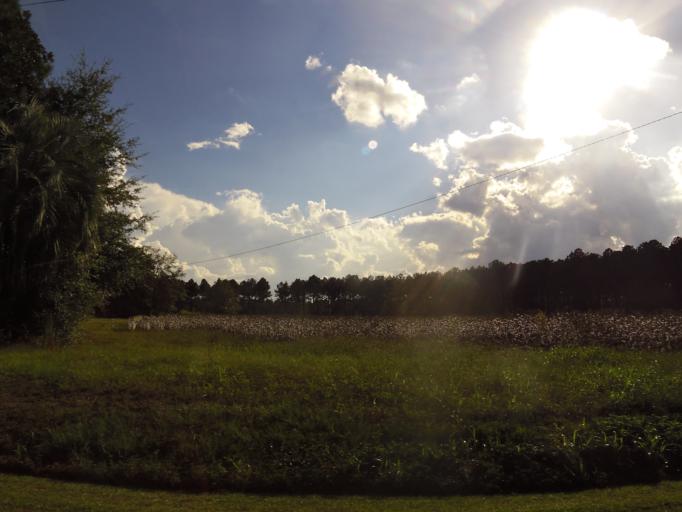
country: US
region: Georgia
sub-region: Brooks County
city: Quitman
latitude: 30.7828
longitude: -83.6221
